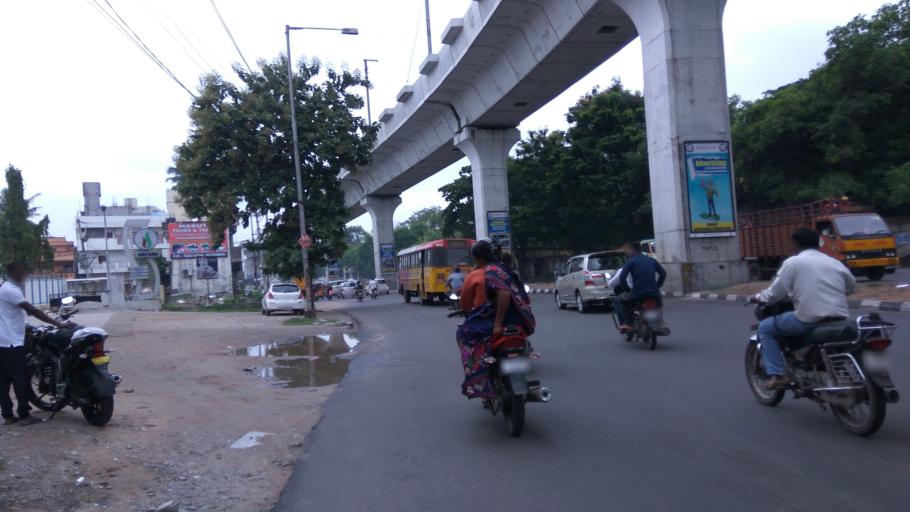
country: IN
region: Telangana
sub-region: Hyderabad
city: Malkajgiri
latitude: 17.4369
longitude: 78.5170
